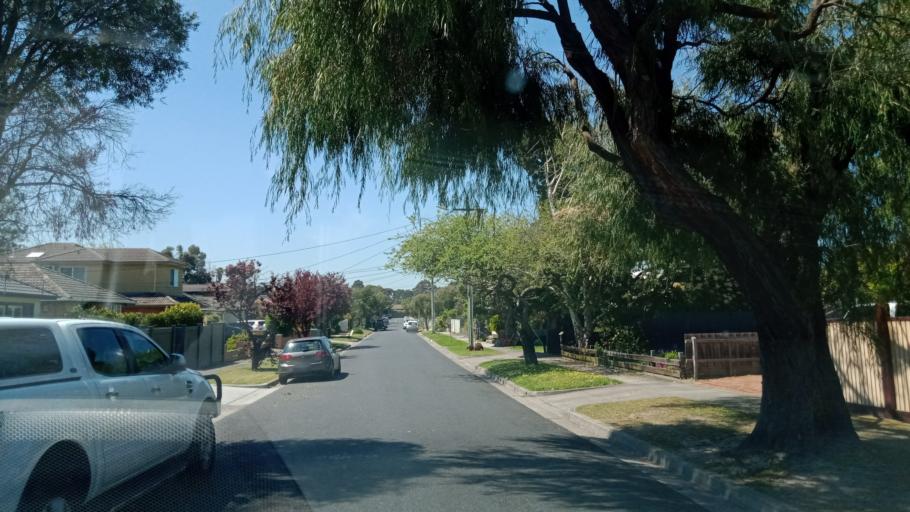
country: AU
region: Victoria
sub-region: Monash
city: Oakleigh South
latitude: -37.9301
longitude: 145.0785
